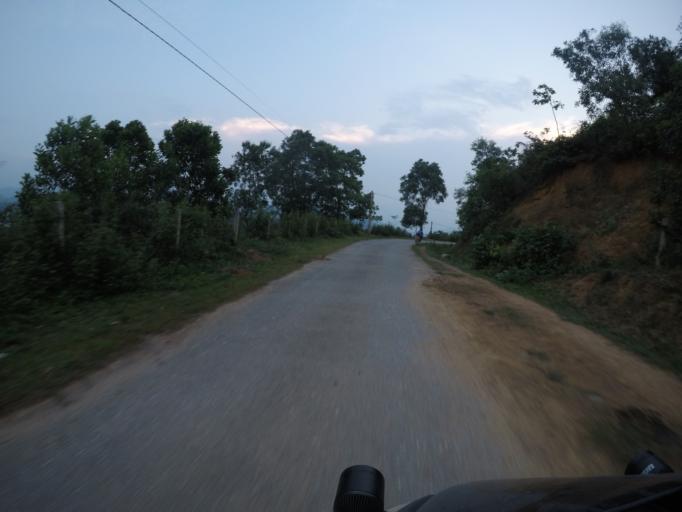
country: VN
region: Thai Nguyen
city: Chua Hang
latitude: 21.5830
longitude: 105.7087
